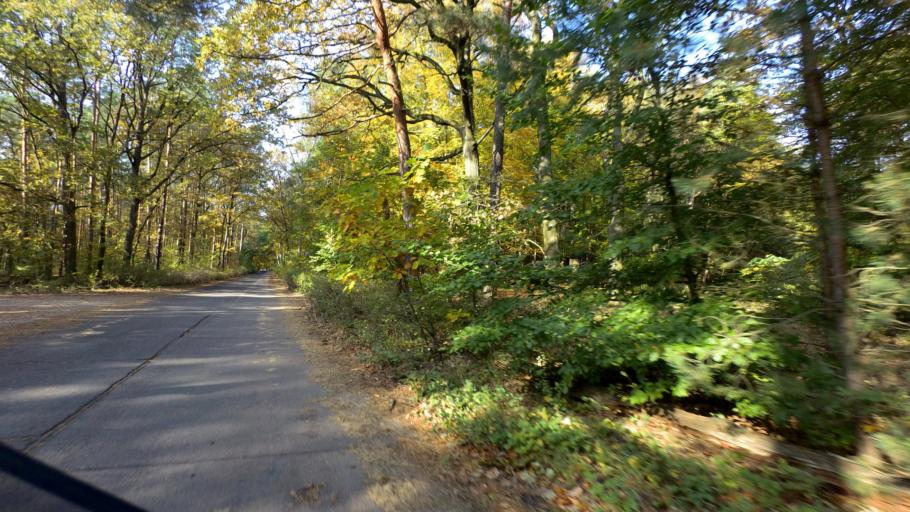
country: DE
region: Berlin
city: Friedrichshagen
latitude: 52.4191
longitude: 13.6143
